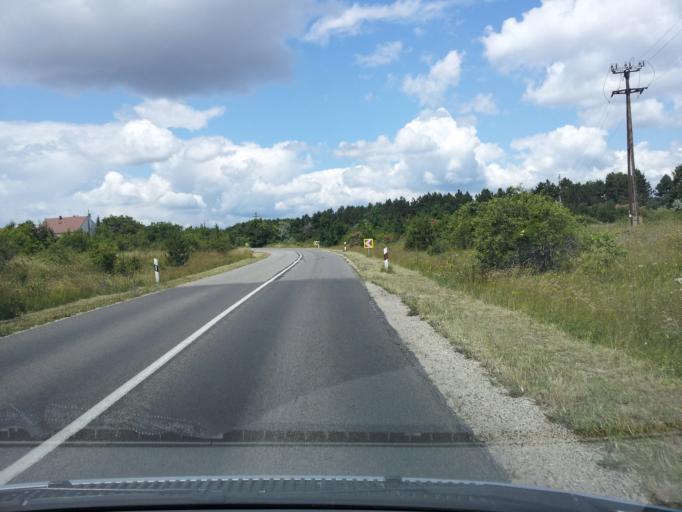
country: HU
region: Veszprem
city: Szentkiralyszabadja
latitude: 47.0614
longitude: 17.9734
